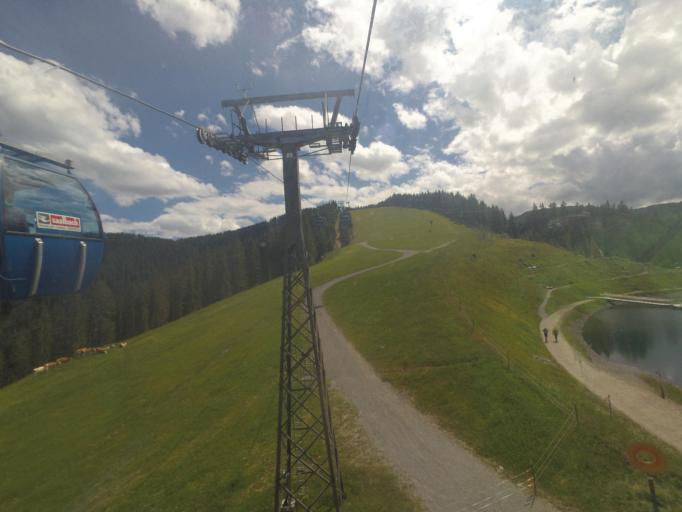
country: AT
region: Salzburg
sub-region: Politischer Bezirk Zell am See
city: Leogang
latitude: 47.4254
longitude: 12.7140
